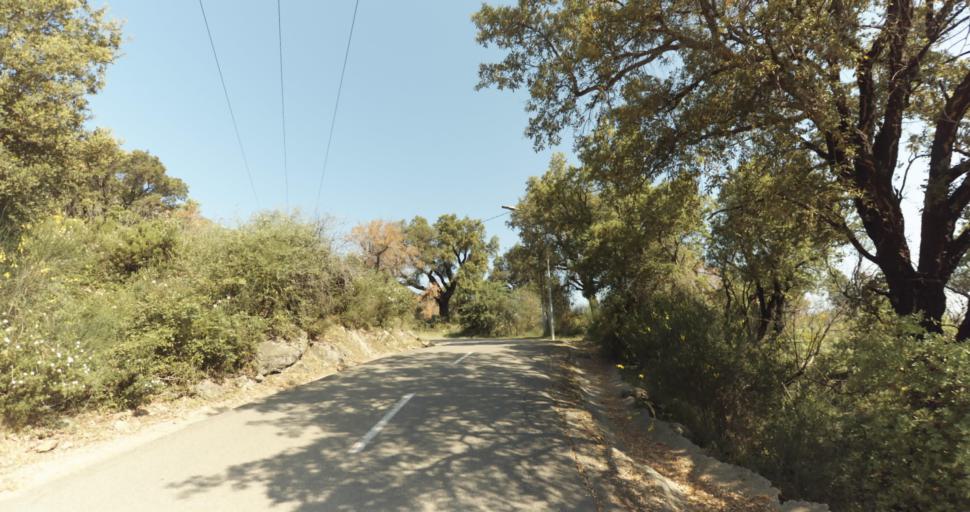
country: FR
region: Corsica
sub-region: Departement de la Haute-Corse
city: Biguglia
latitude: 42.6220
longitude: 9.4222
